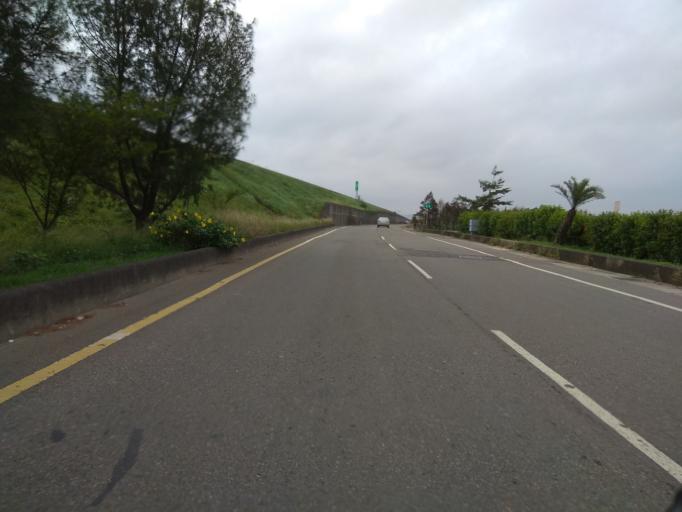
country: TW
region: Taiwan
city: Taoyuan City
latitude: 24.9694
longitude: 121.1336
